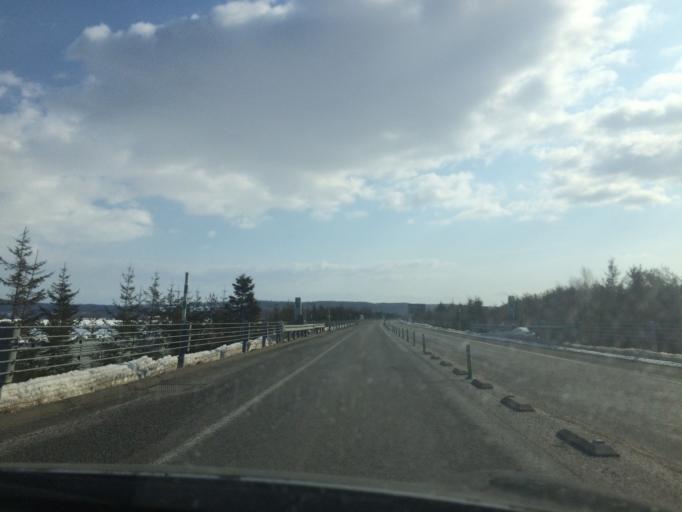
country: JP
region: Hokkaido
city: Chitose
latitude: 42.8839
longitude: 141.6902
